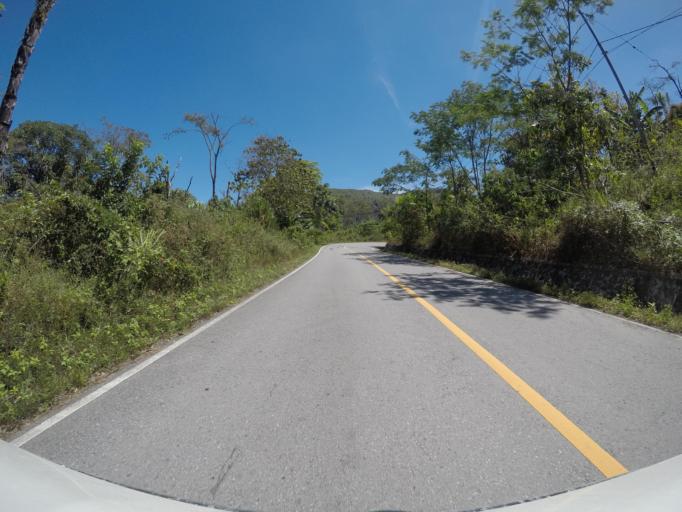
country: TL
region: Manatuto
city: Manatuto
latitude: -8.7741
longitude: 125.9648
